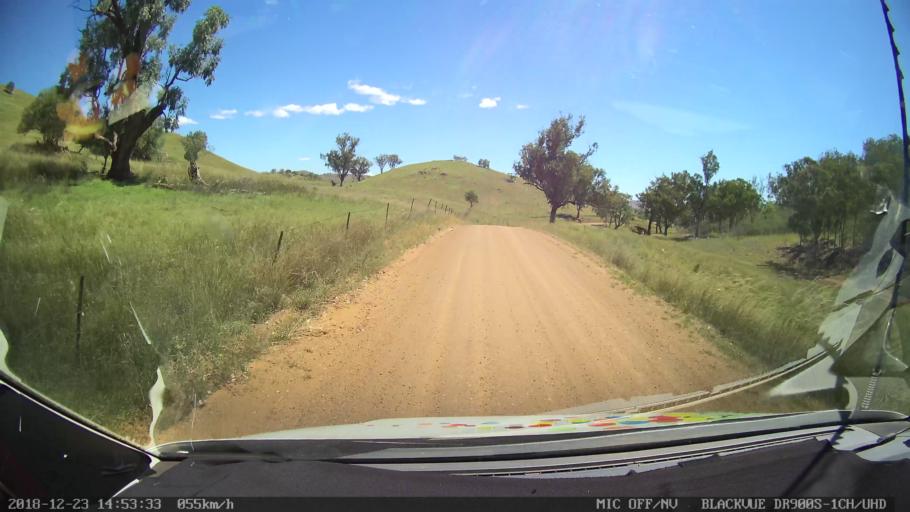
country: AU
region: New South Wales
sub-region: Tamworth Municipality
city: Manilla
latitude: -30.6919
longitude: 150.8513
